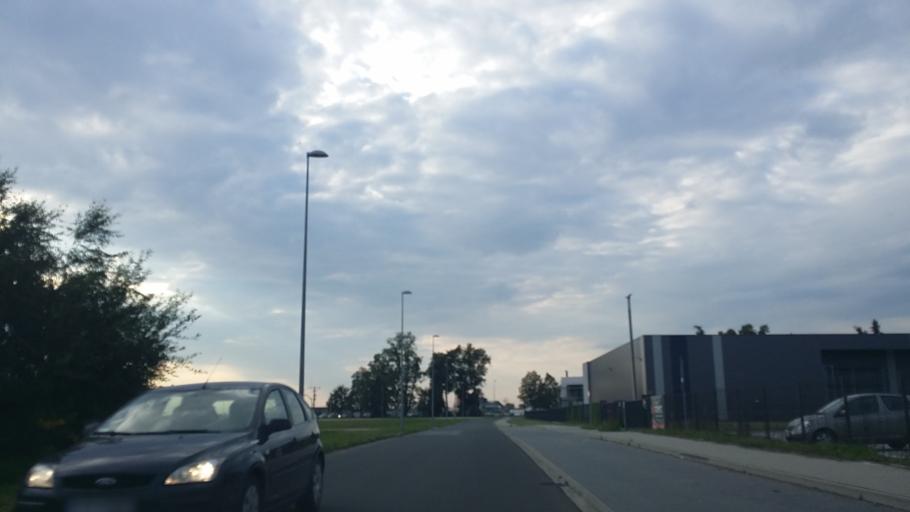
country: PL
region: Lesser Poland Voivodeship
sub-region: Powiat oswiecimski
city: Zator
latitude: 49.9962
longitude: 19.4161
